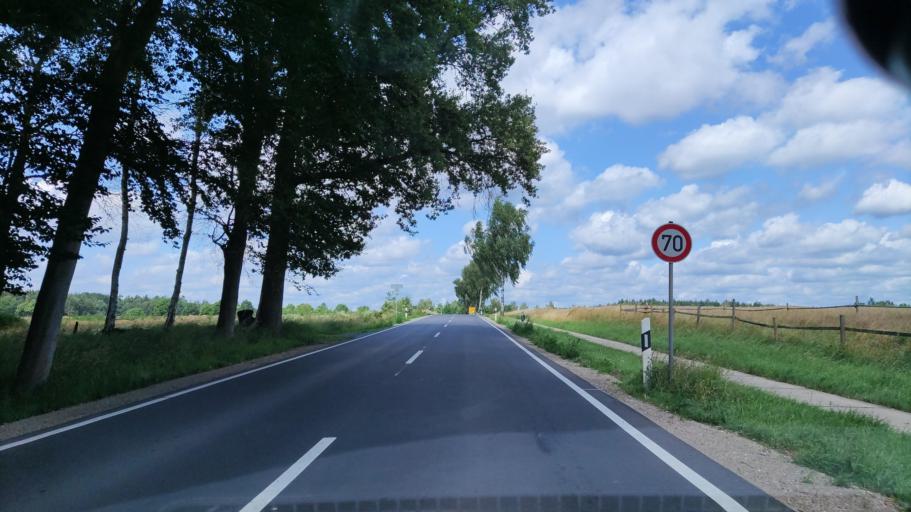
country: DE
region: Lower Saxony
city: Bomlitz
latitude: 52.9014
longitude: 9.6158
